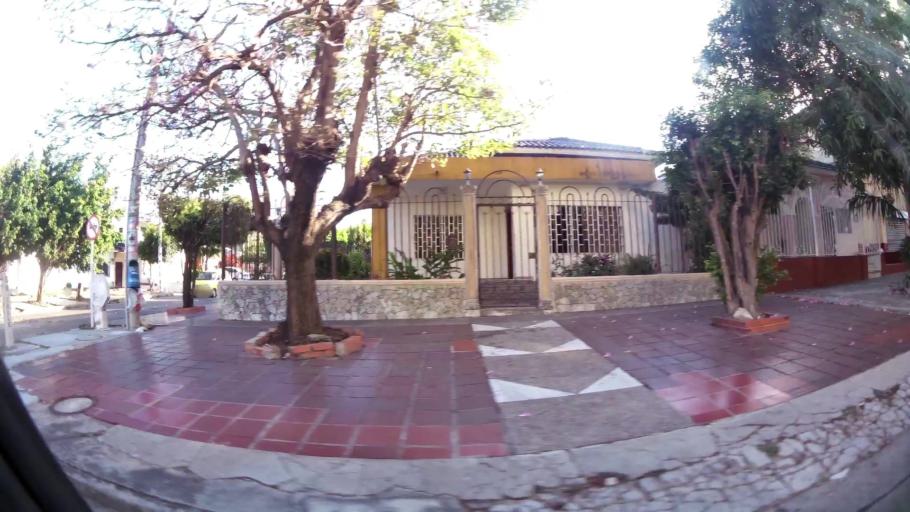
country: CO
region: Atlantico
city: Barranquilla
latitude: 10.9866
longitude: -74.8033
